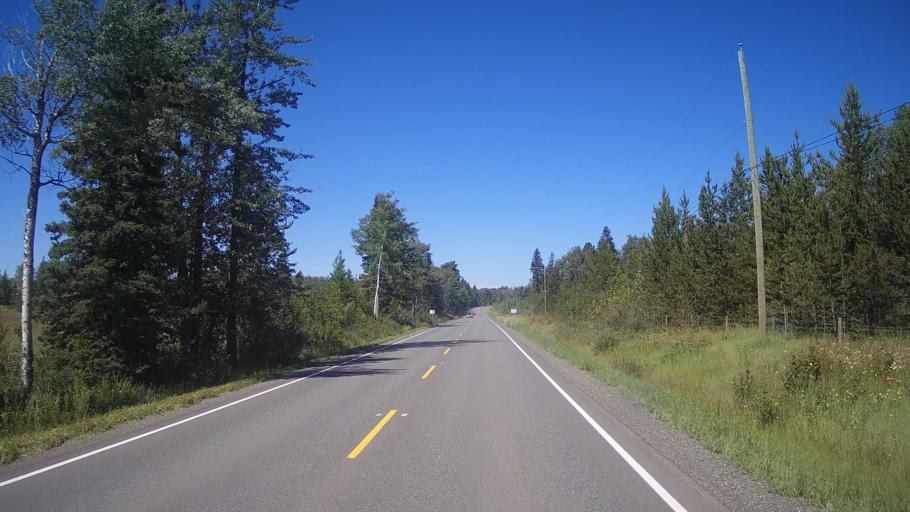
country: CA
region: British Columbia
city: Cache Creek
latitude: 51.5402
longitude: -121.0391
